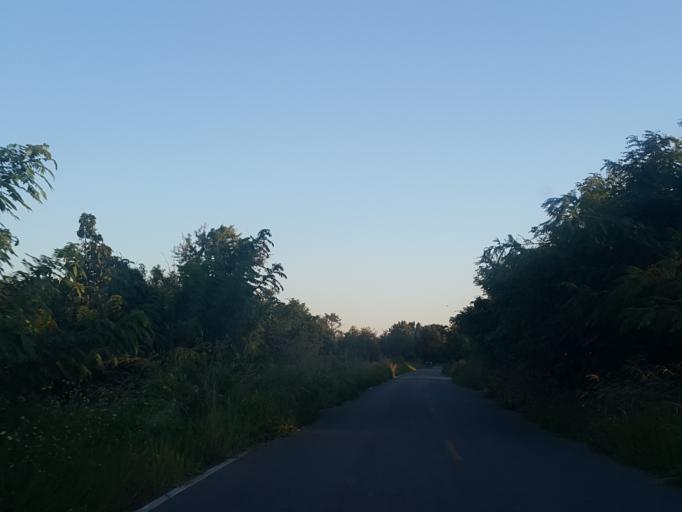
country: TH
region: Chiang Mai
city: San Sai
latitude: 18.8506
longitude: 99.1469
